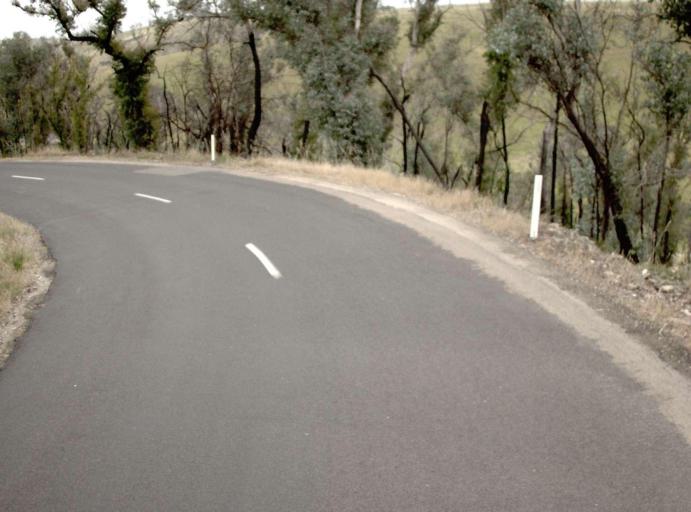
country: AU
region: Victoria
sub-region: Wellington
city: Heyfield
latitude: -37.8477
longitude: 146.7077
